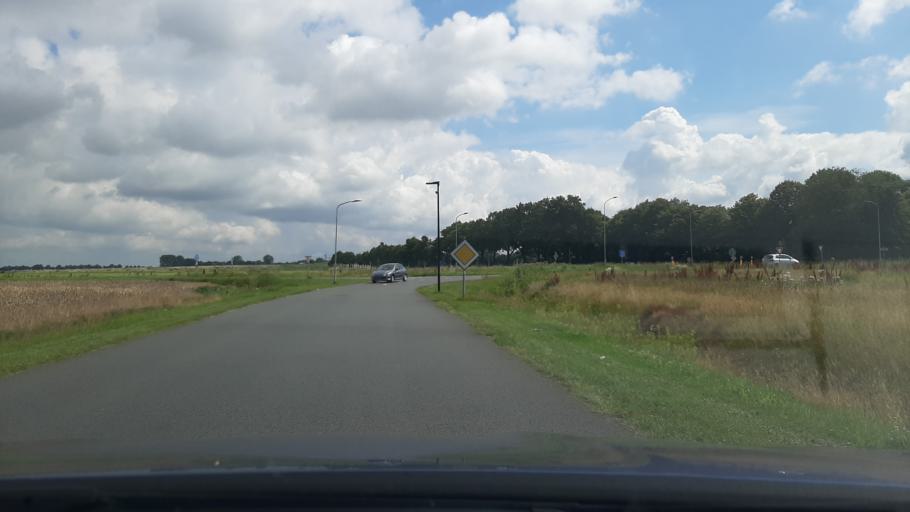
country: NL
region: Groningen
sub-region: Gemeente  Oldambt
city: Winschoten
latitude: 53.1815
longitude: 6.9656
